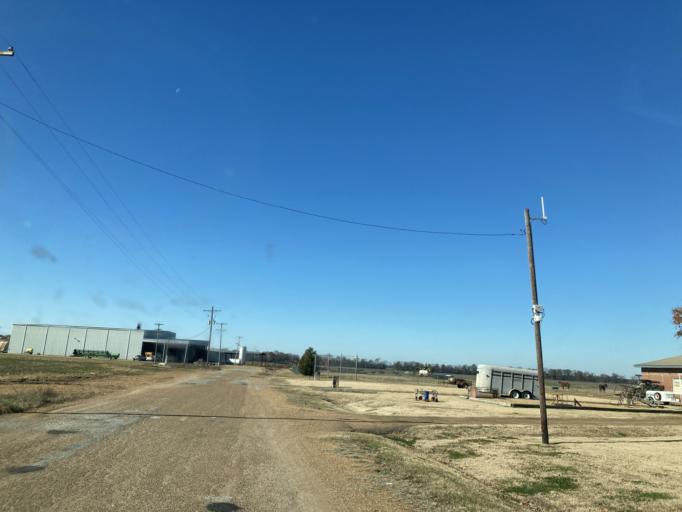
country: US
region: Mississippi
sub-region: Sharkey County
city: Rolling Fork
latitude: 32.8251
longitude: -90.7078
